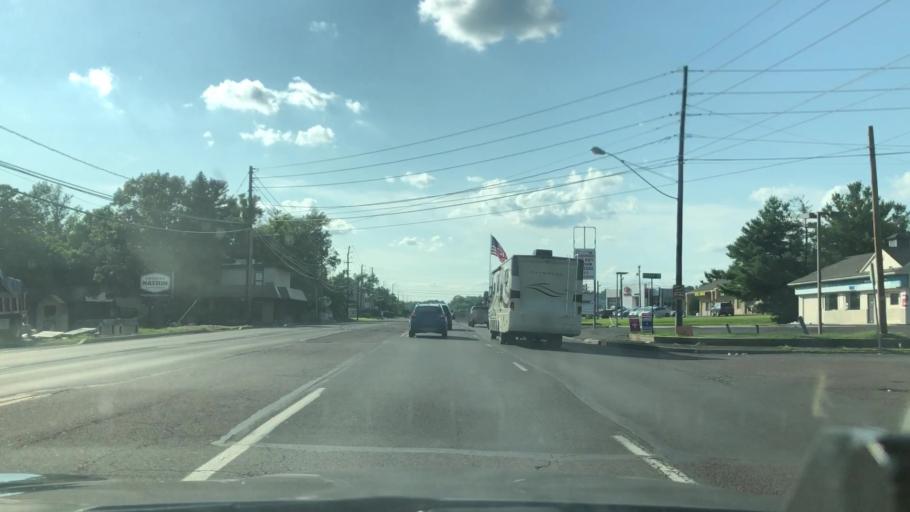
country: US
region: Pennsylvania
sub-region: Montgomery County
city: Hatfield
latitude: 40.2994
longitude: -75.2856
